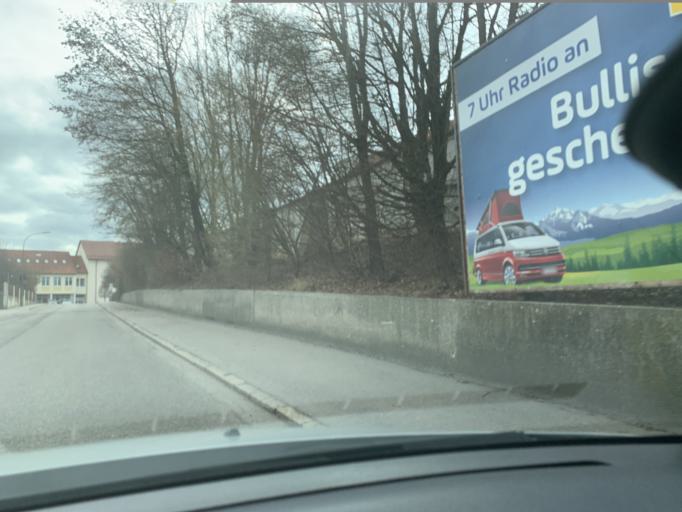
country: DE
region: Bavaria
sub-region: Lower Bavaria
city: Vilsbiburg
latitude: 48.4530
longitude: 12.3565
